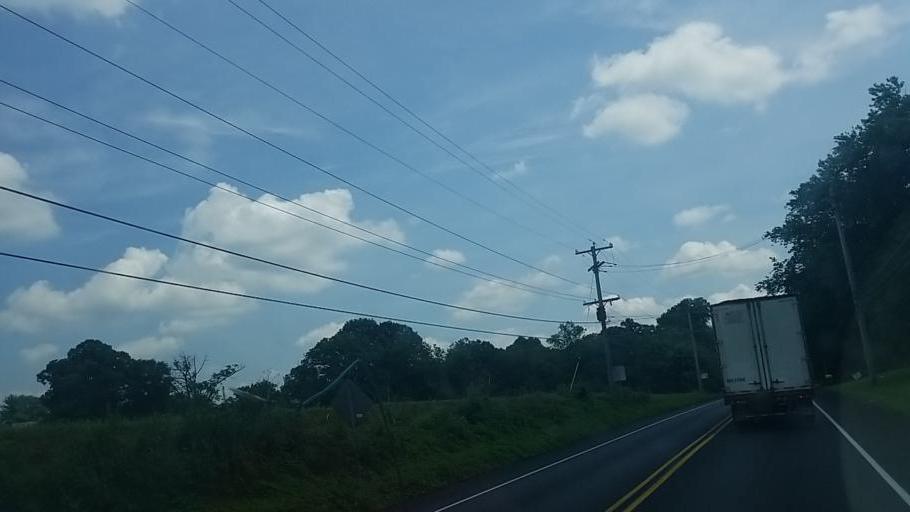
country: US
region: Pennsylvania
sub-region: Chester County
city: Toughkenamon
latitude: 39.8143
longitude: -75.7632
